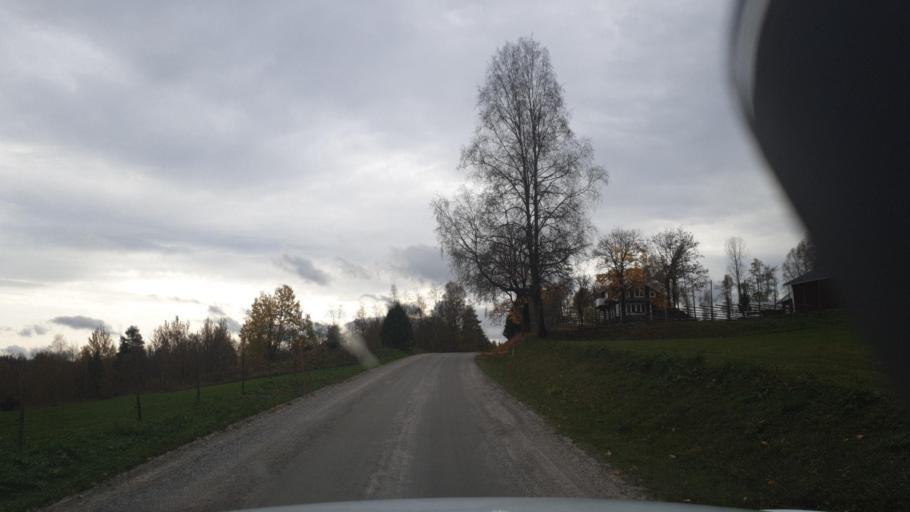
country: SE
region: Vaermland
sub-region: Arvika Kommun
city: Arvika
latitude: 59.8310
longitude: 12.7475
